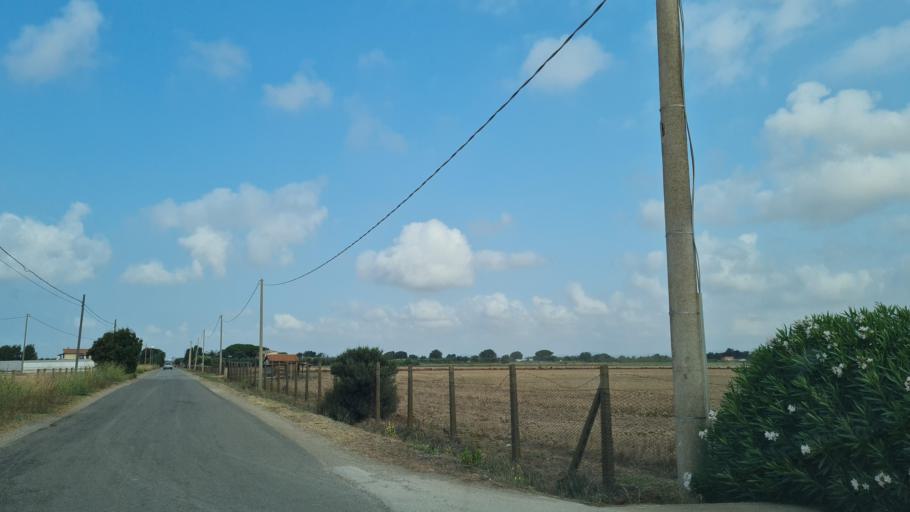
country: IT
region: Latium
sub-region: Provincia di Viterbo
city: Montalto di Castro
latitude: 42.3129
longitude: 11.6140
